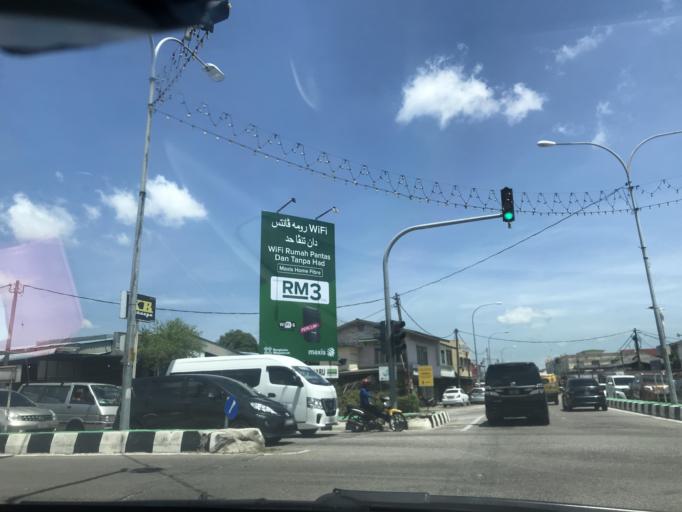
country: MY
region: Kelantan
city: Kota Bharu
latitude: 6.1248
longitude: 102.2578
